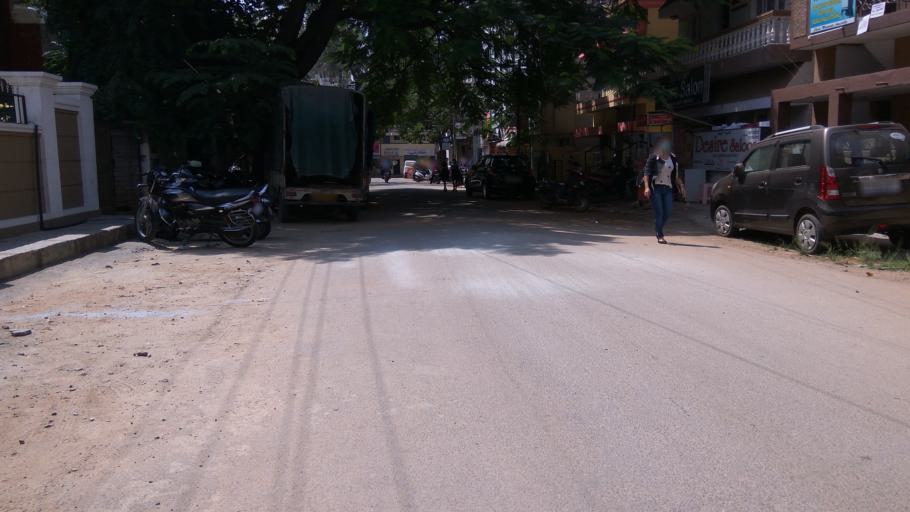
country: IN
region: Karnataka
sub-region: Bangalore Urban
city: Bangalore
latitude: 12.9753
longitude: 77.6390
